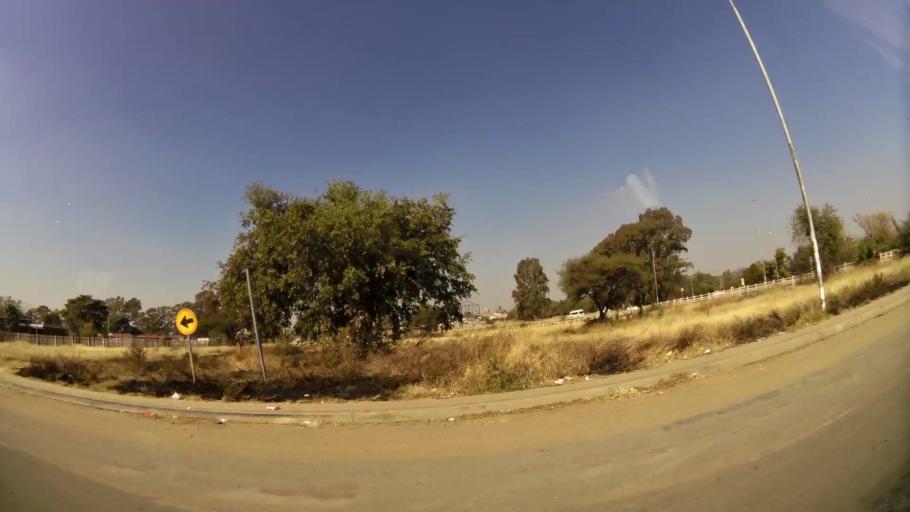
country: ZA
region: North-West
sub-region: Bojanala Platinum District Municipality
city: Rustenburg
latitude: -25.6608
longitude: 27.2310
